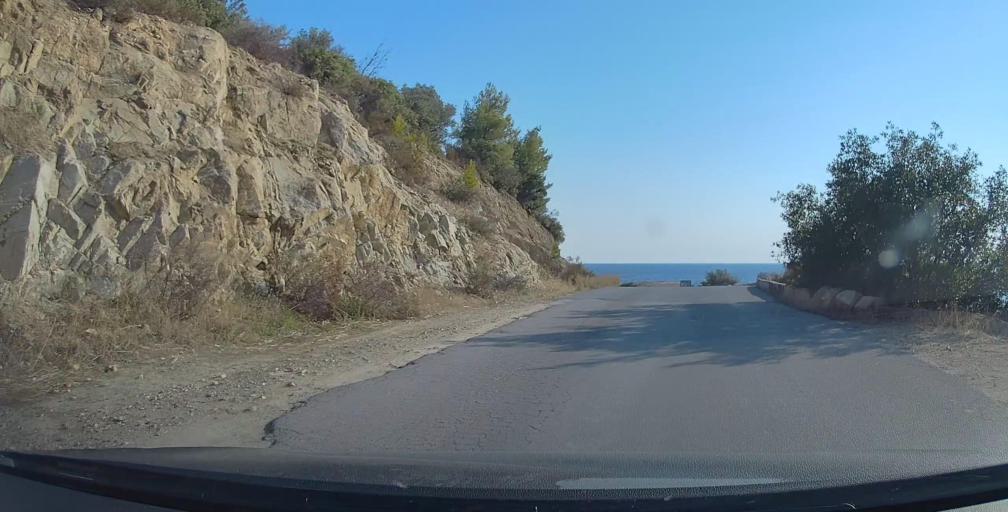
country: GR
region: Central Macedonia
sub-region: Nomos Chalkidikis
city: Sykia
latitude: 39.9932
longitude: 23.8928
